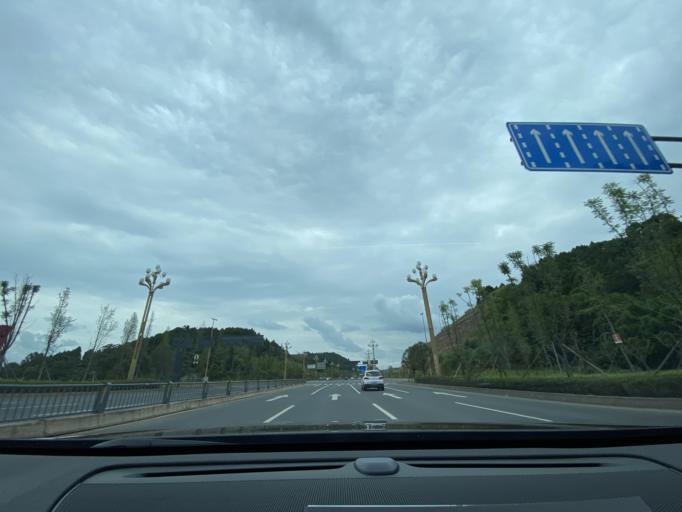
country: CN
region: Sichuan
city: Jiancheng
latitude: 30.4685
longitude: 104.4942
